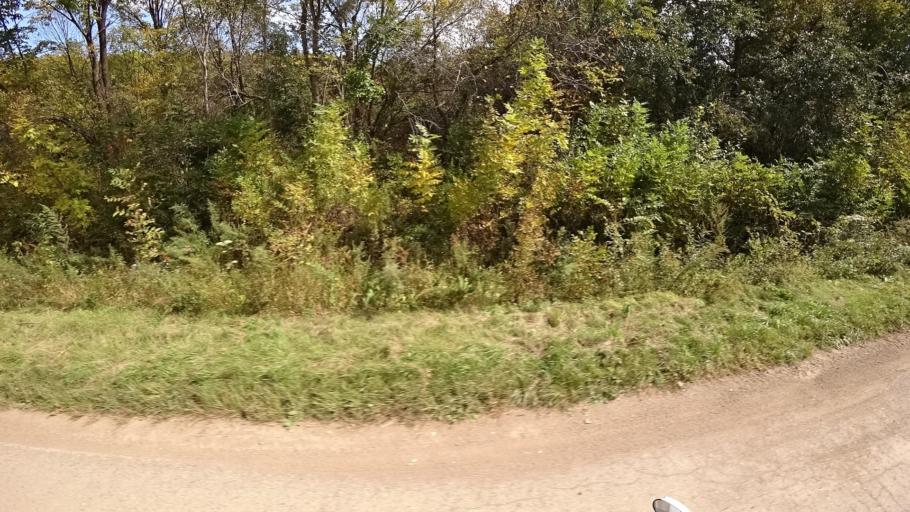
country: RU
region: Primorskiy
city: Yakovlevka
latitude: 44.7469
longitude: 133.6058
